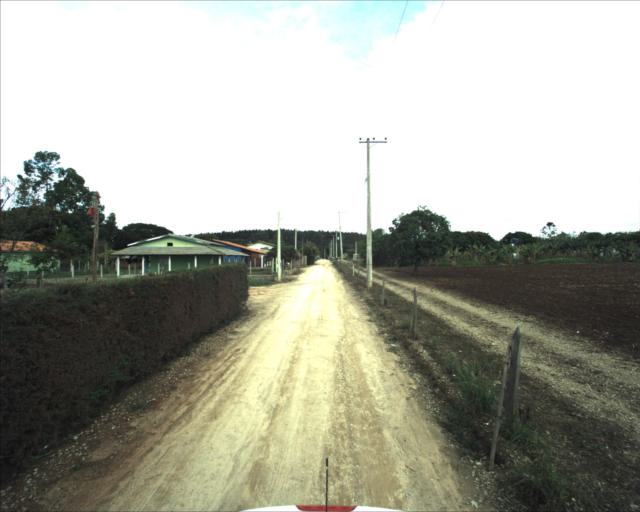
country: BR
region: Sao Paulo
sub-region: Aracoiaba Da Serra
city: Aracoiaba da Serra
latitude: -23.5503
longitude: -47.5467
